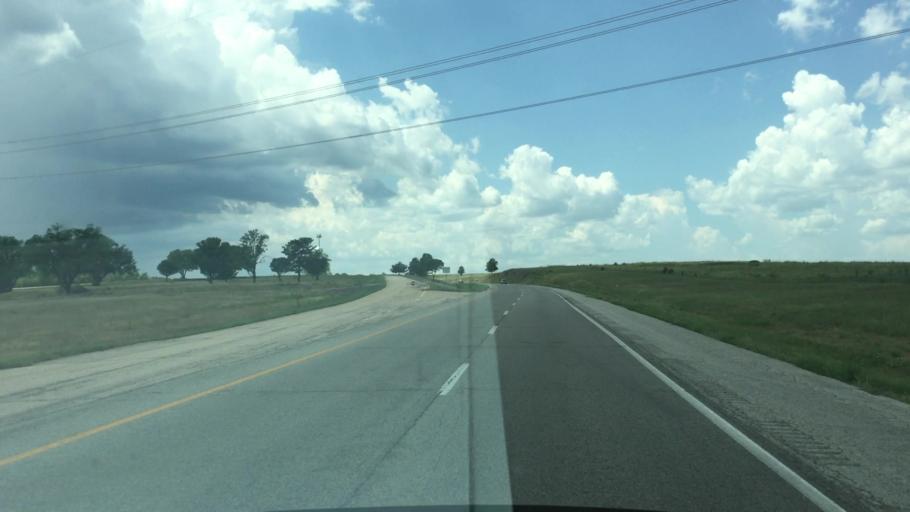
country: US
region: Kansas
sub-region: Shawnee County
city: Topeka
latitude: 39.0314
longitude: -95.5975
